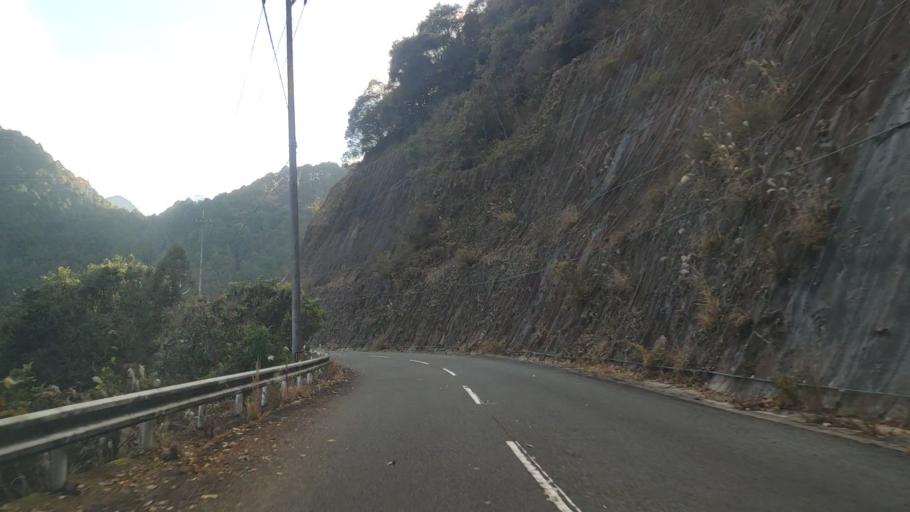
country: JP
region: Ehime
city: Saijo
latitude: 33.8685
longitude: 133.1623
